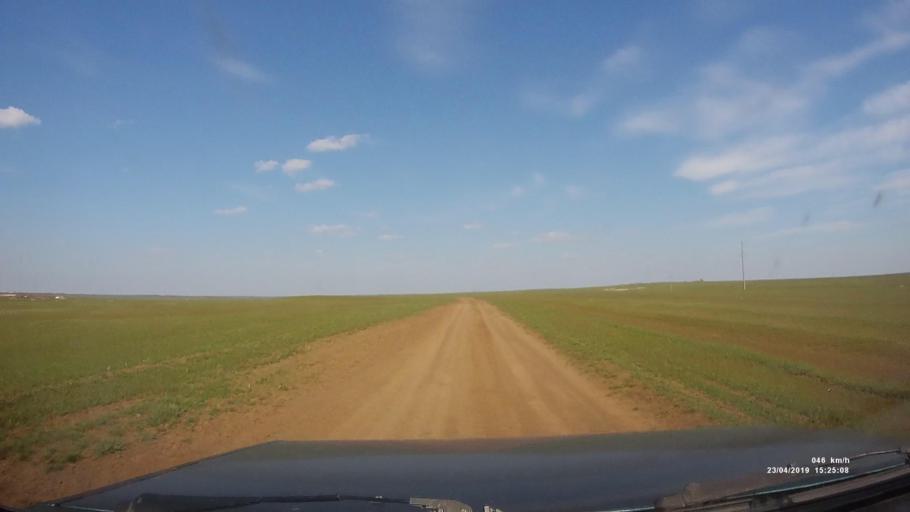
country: RU
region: Rostov
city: Remontnoye
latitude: 46.5409
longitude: 42.9782
